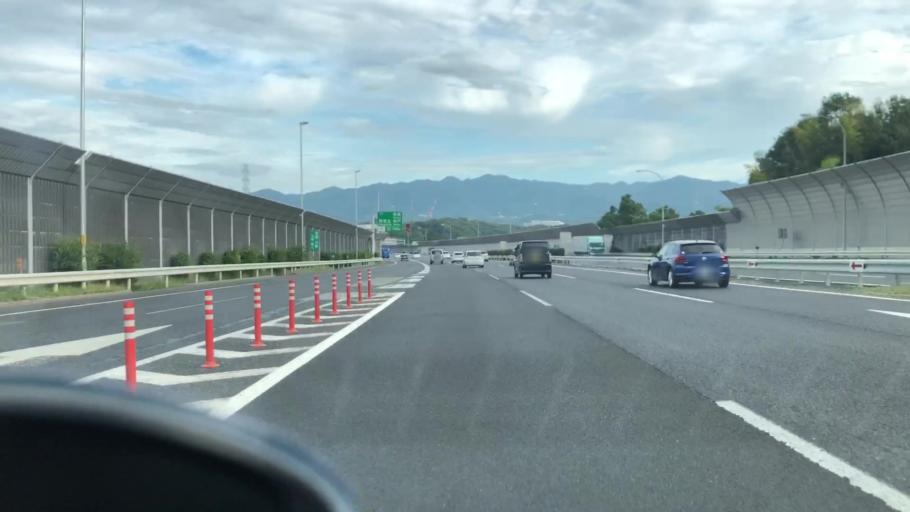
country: JP
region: Hyogo
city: Sandacho
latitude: 34.8444
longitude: 135.2262
